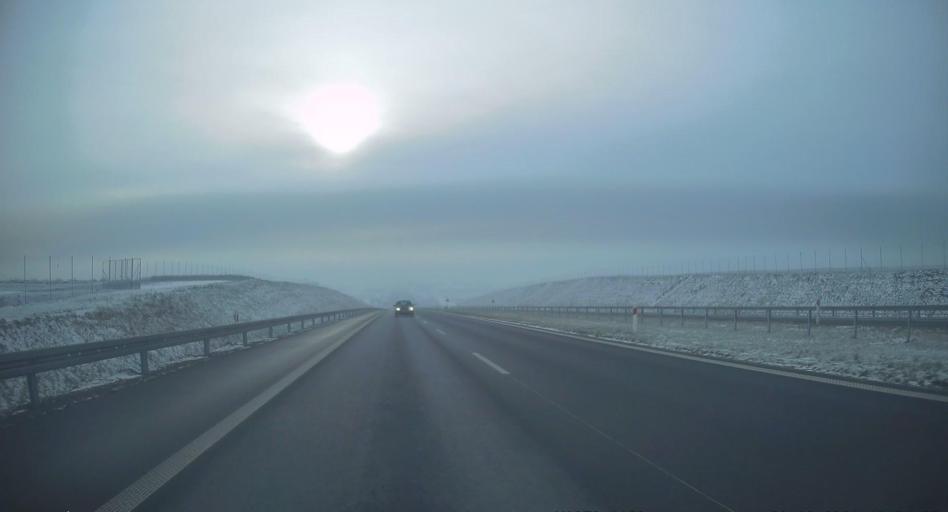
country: PL
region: Lesser Poland Voivodeship
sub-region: Powiat miechowski
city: Miechow
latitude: 50.2889
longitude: 20.0244
